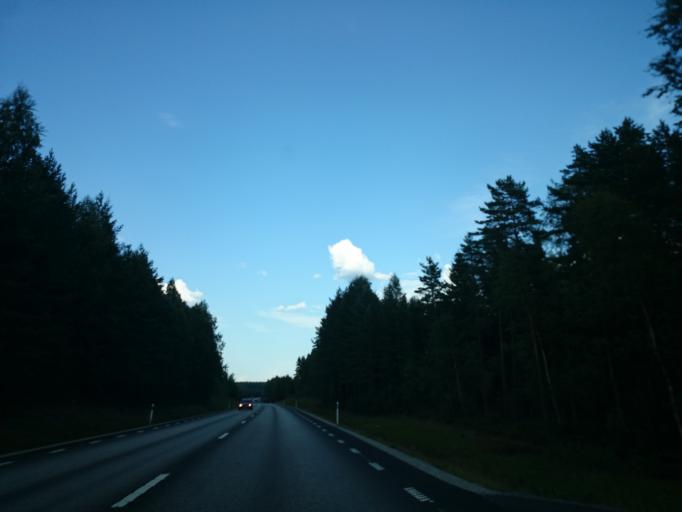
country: SE
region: OErebro
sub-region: Lindesbergs Kommun
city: Lindesberg
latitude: 59.6810
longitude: 15.3177
